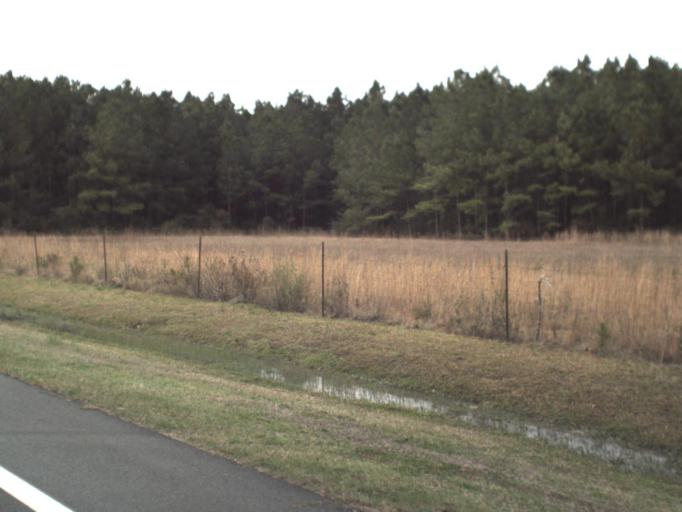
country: US
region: Florida
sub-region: Gulf County
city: Wewahitchka
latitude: 30.1199
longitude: -85.2125
